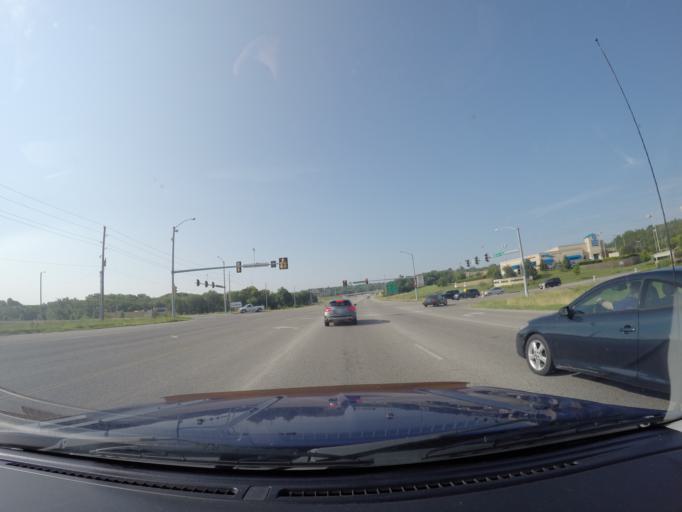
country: US
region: Kansas
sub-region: Riley County
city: Manhattan
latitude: 39.1739
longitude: -96.6037
